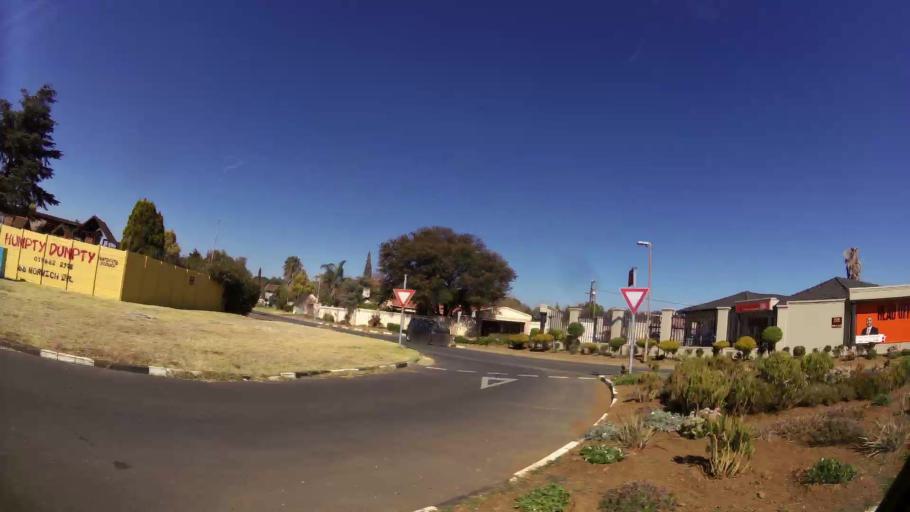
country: ZA
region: Gauteng
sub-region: City of Johannesburg Metropolitan Municipality
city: Johannesburg
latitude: -26.2866
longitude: 28.0579
